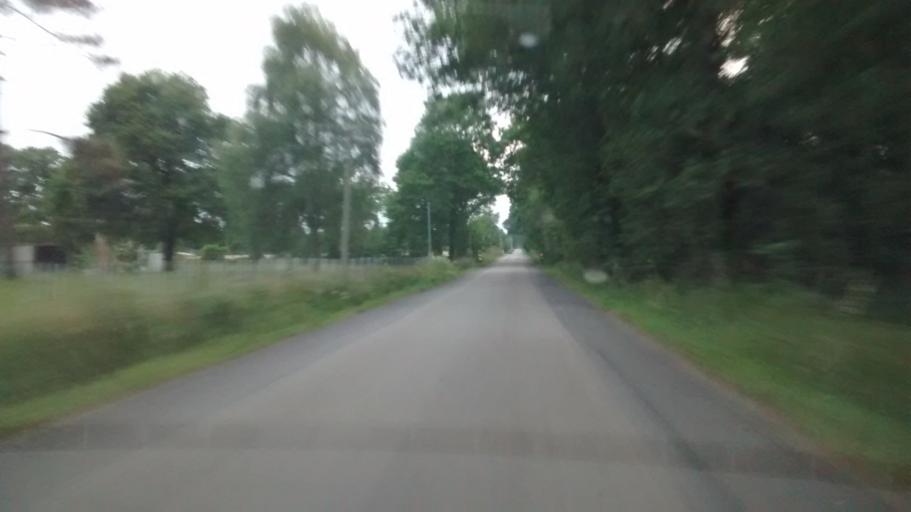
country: FR
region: Brittany
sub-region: Departement du Morbihan
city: Pluherlin
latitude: 47.7339
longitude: -2.3284
